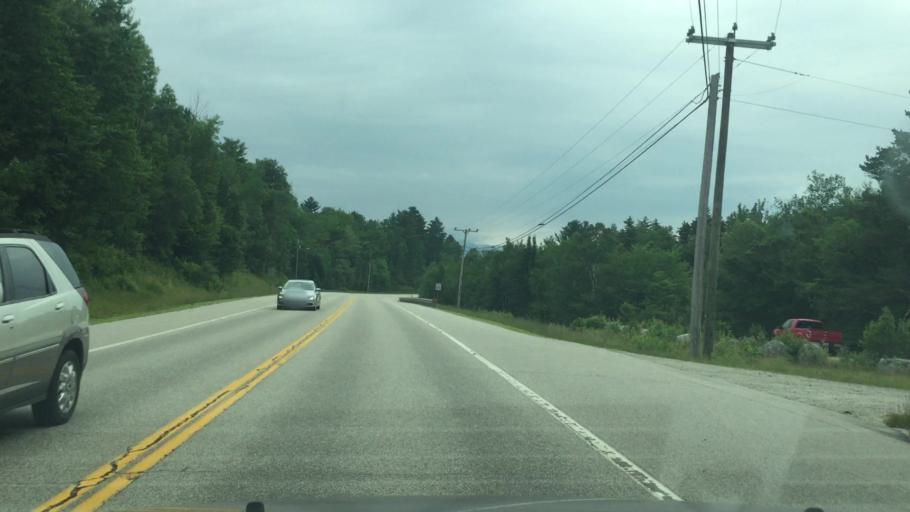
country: US
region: New Hampshire
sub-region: Grafton County
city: Deerfield
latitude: 44.2691
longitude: -71.5340
